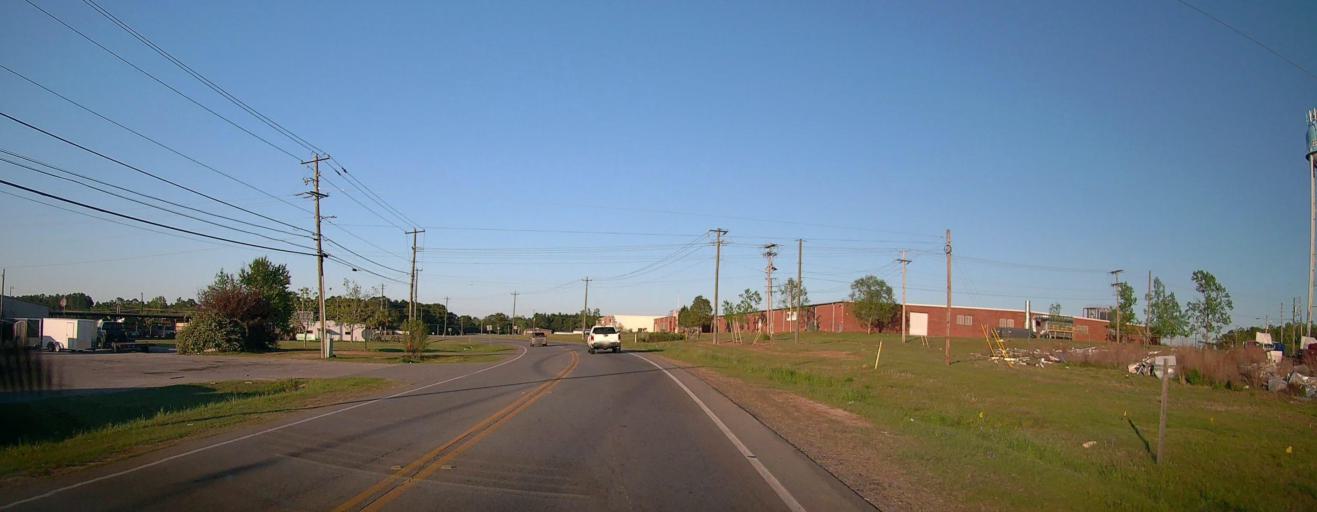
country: US
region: Georgia
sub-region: Ben Hill County
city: Fitzgerald
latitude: 31.6944
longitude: -83.2412
